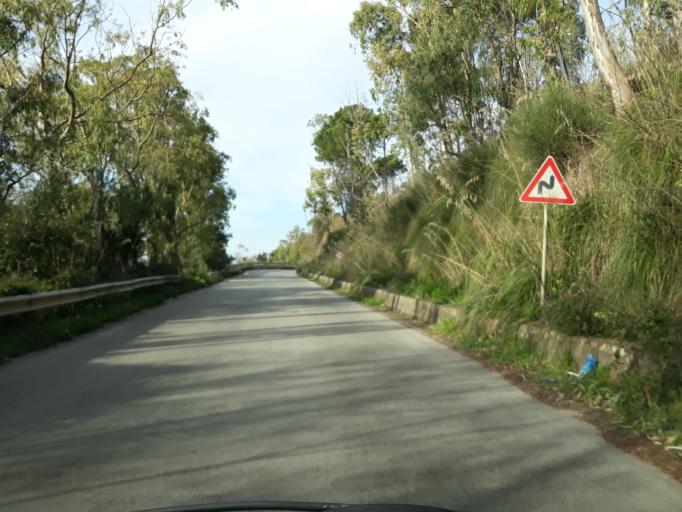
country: IT
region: Sicily
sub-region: Palermo
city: Torretta
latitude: 38.1137
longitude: 13.2415
